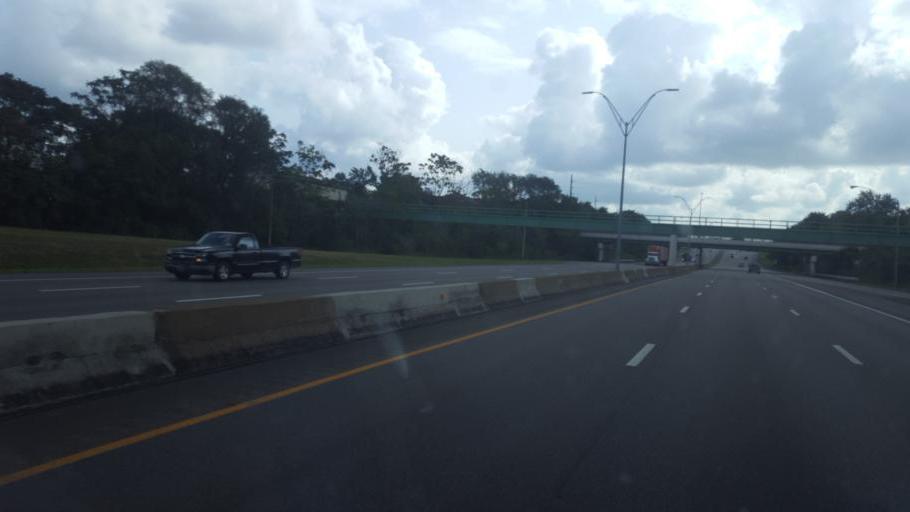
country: US
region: Ohio
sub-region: Stark County
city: Canton
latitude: 40.7846
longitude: -81.3967
